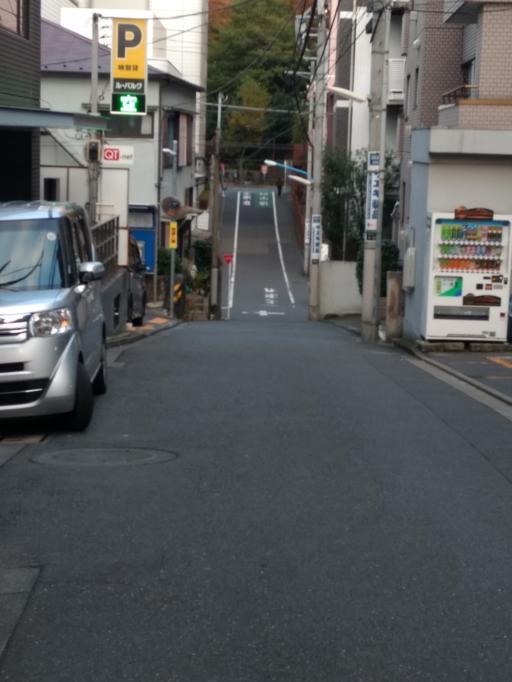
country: JP
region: Tokyo
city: Tokyo
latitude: 35.6885
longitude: 139.6873
